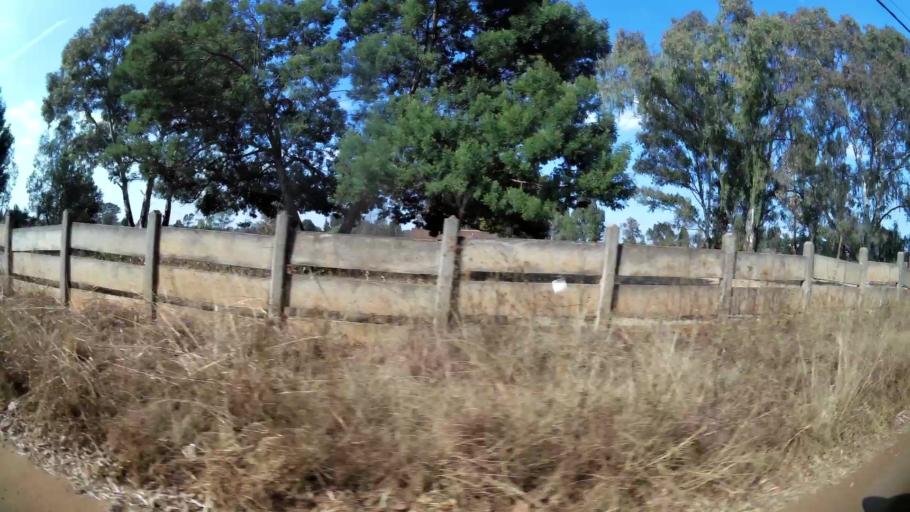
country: ZA
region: Gauteng
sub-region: Ekurhuleni Metropolitan Municipality
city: Benoni
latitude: -26.1092
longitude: 28.3604
